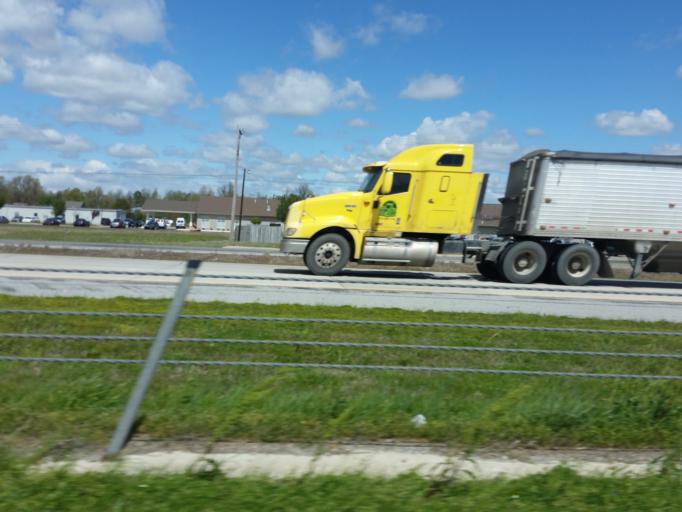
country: US
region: Arkansas
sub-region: Craighead County
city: Jonesboro
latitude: 35.8070
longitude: -90.6634
